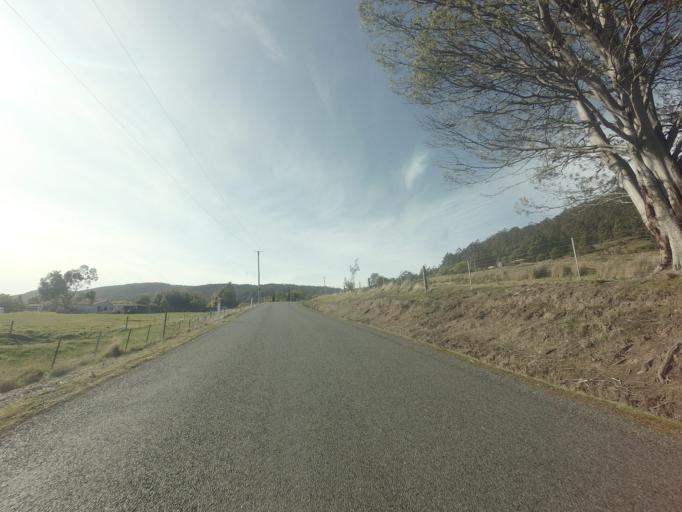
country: AU
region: Tasmania
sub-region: Kingborough
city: Kettering
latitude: -43.1701
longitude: 147.1750
